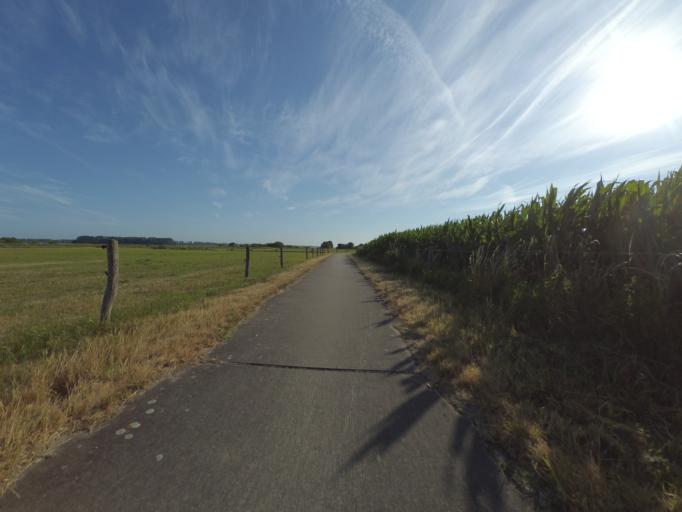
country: NL
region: Gelderland
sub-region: Gemeente Nunspeet
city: Nunspeet
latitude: 52.3968
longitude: 5.7413
